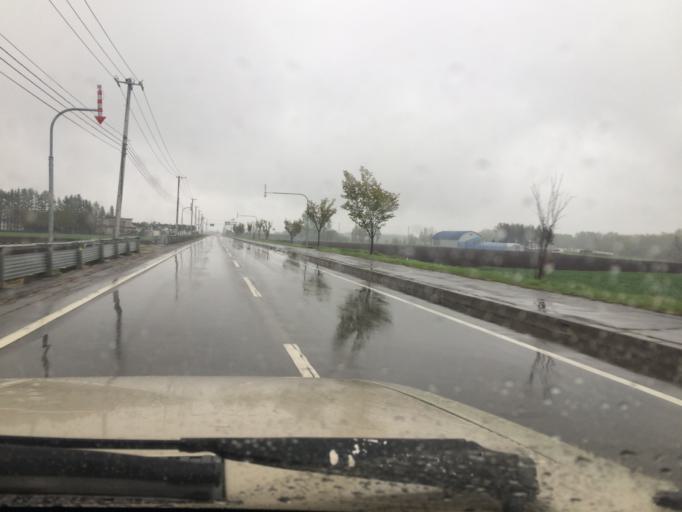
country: JP
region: Hokkaido
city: Obihiro
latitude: 42.8874
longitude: 143.0369
